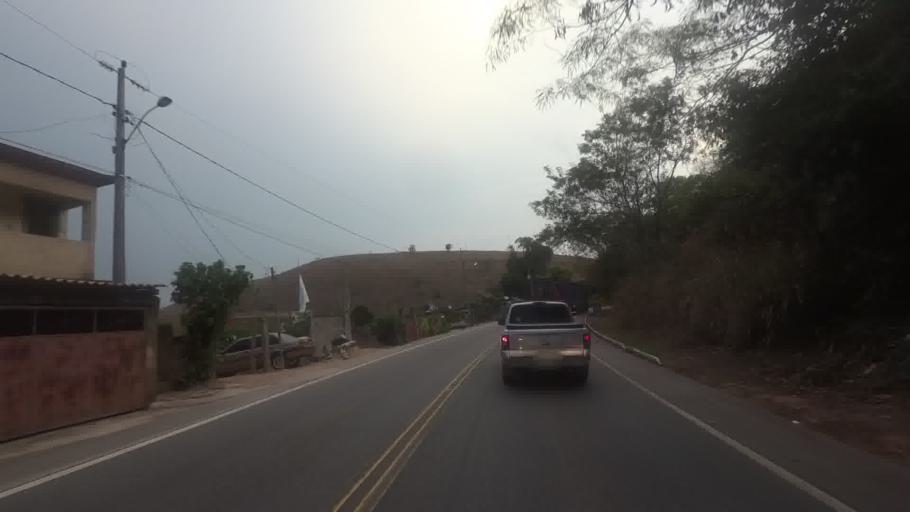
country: BR
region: Rio de Janeiro
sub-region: Carmo
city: Carmo
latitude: -21.8168
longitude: -42.5976
